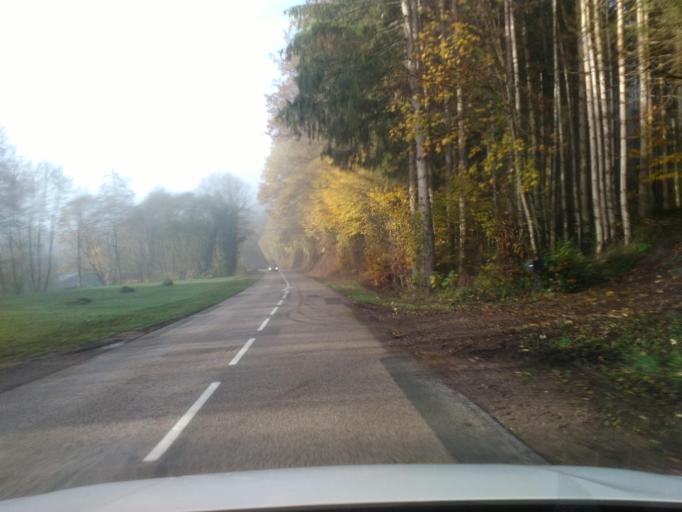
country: FR
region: Lorraine
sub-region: Departement des Vosges
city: Senones
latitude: 48.4201
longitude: 7.0060
